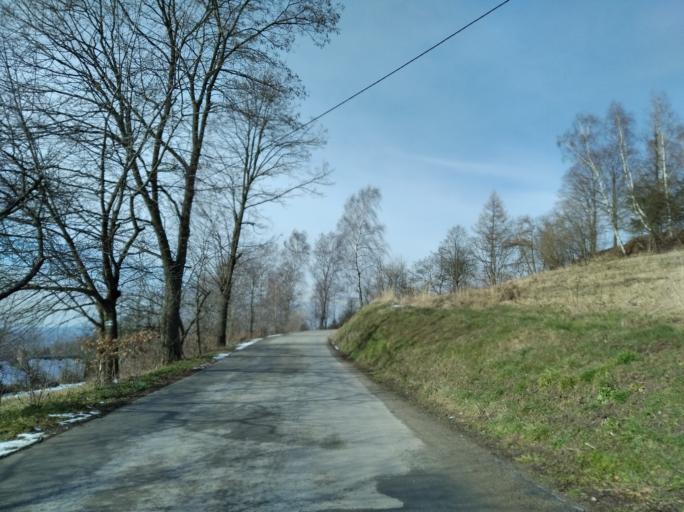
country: PL
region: Subcarpathian Voivodeship
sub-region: Powiat krosnienski
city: Korczyna
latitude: 49.7385
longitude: 21.7856
